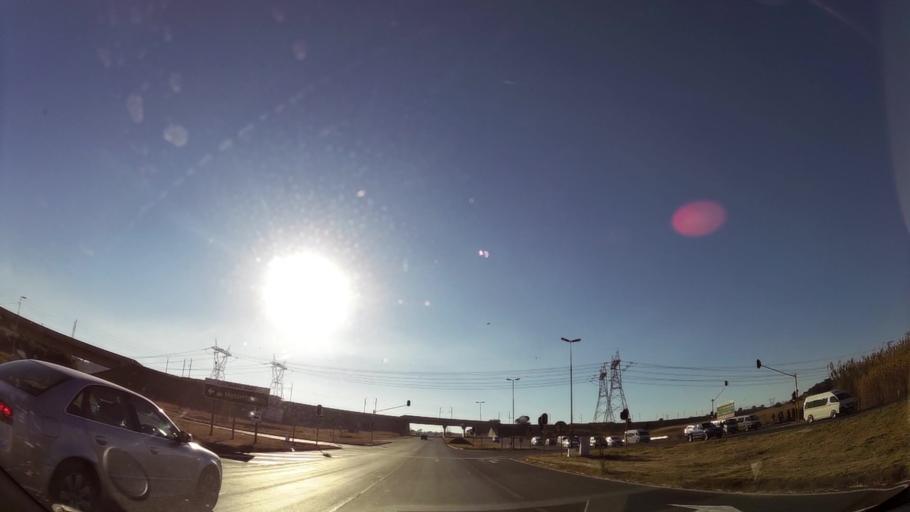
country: ZA
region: Gauteng
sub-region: City of Johannesburg Metropolitan Municipality
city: Modderfontein
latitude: -26.1035
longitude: 28.1762
